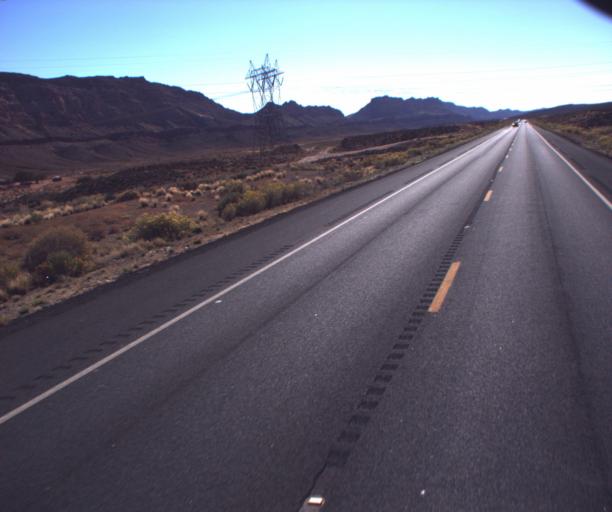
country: US
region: Arizona
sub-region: Coconino County
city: Tuba City
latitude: 36.2906
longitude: -111.4494
